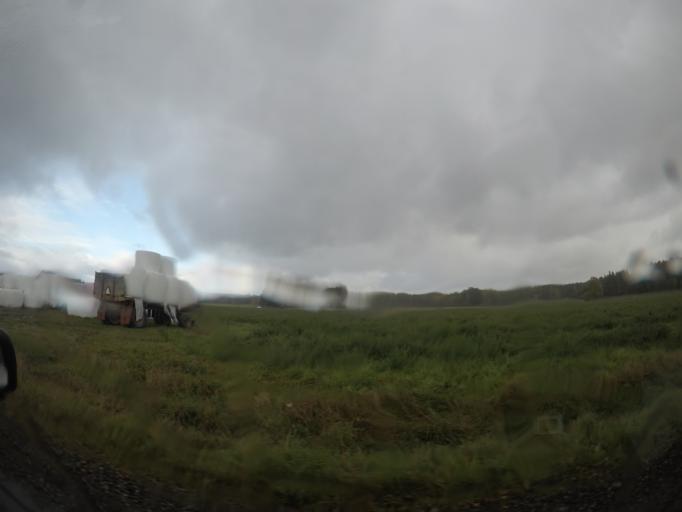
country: SE
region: Soedermanland
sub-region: Eskilstuna Kommun
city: Kvicksund
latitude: 59.3382
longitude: 16.2998
